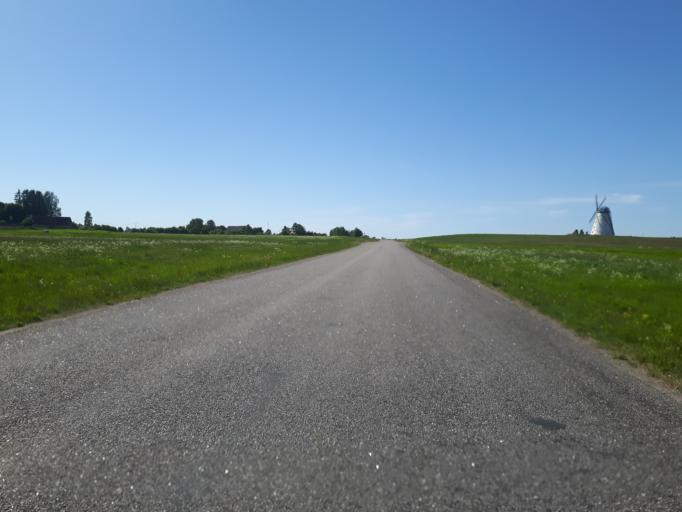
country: EE
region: Laeaene-Virumaa
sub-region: Haljala vald
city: Haljala
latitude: 59.5439
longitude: 26.1800
